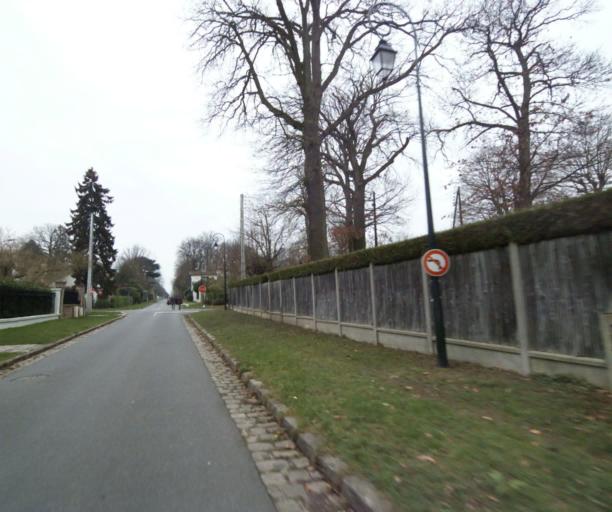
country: FR
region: Ile-de-France
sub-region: Departement des Yvelines
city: La Celle-Saint-Cloud
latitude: 48.8457
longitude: 2.1503
